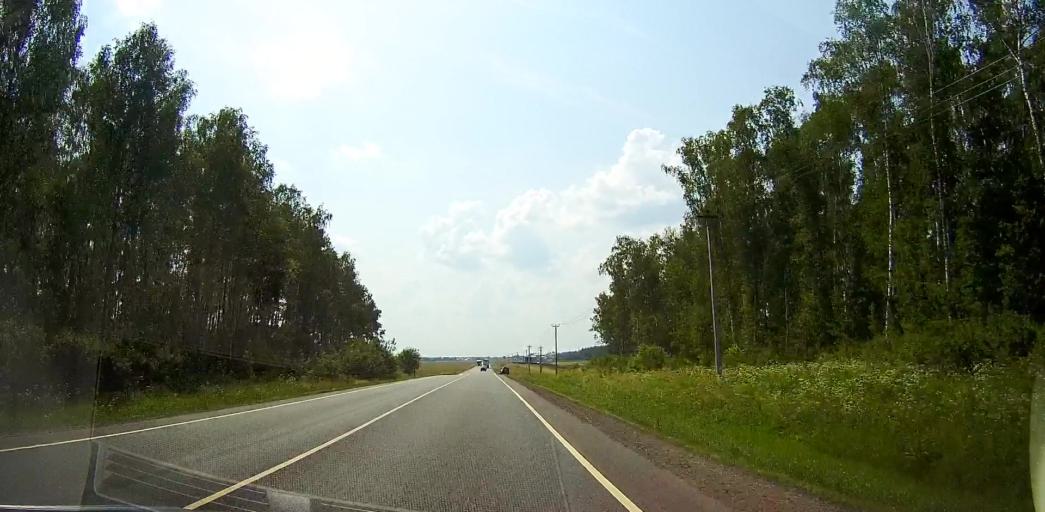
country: RU
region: Moskovskaya
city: Meshcherino
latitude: 55.1587
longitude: 38.3114
